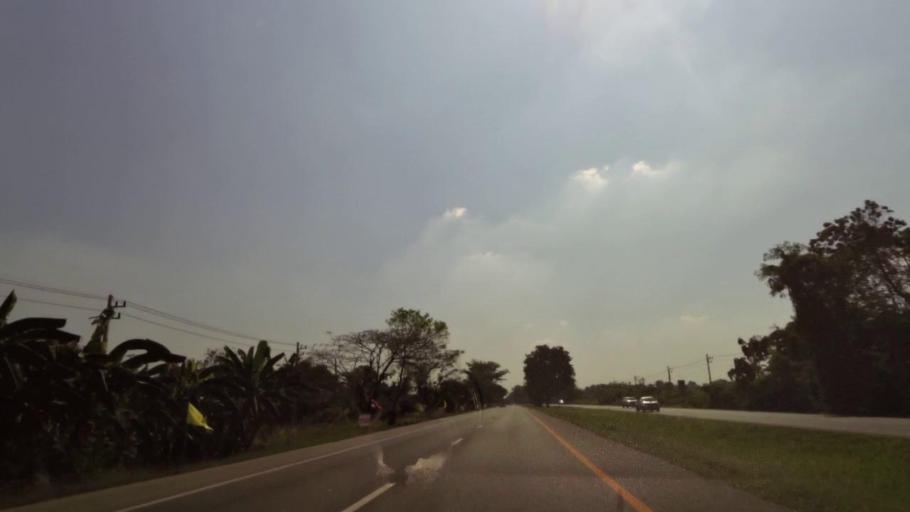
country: TH
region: Phichit
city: Bueng Na Rang
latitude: 16.2380
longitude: 100.1254
